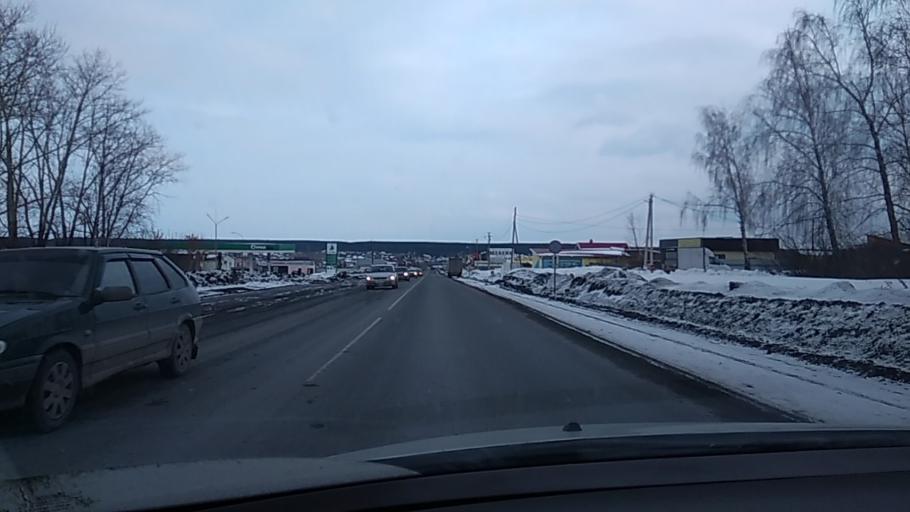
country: RU
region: Sverdlovsk
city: Dvurechensk
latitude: 56.6393
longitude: 61.2313
